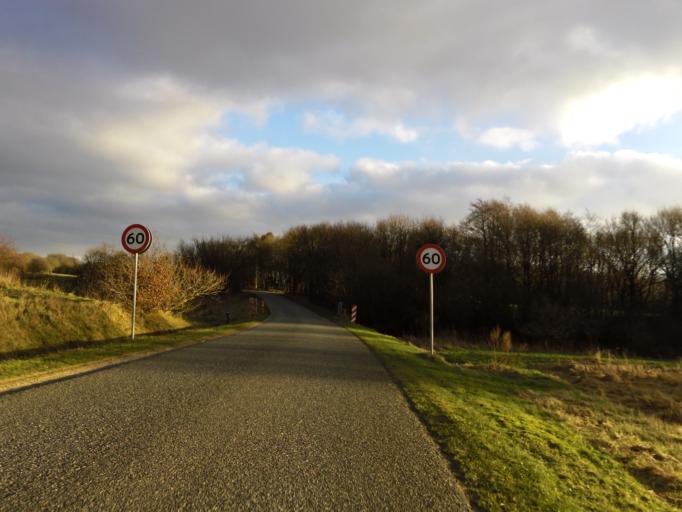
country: DK
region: South Denmark
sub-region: Esbjerg Kommune
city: Ribe
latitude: 55.2953
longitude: 8.8567
